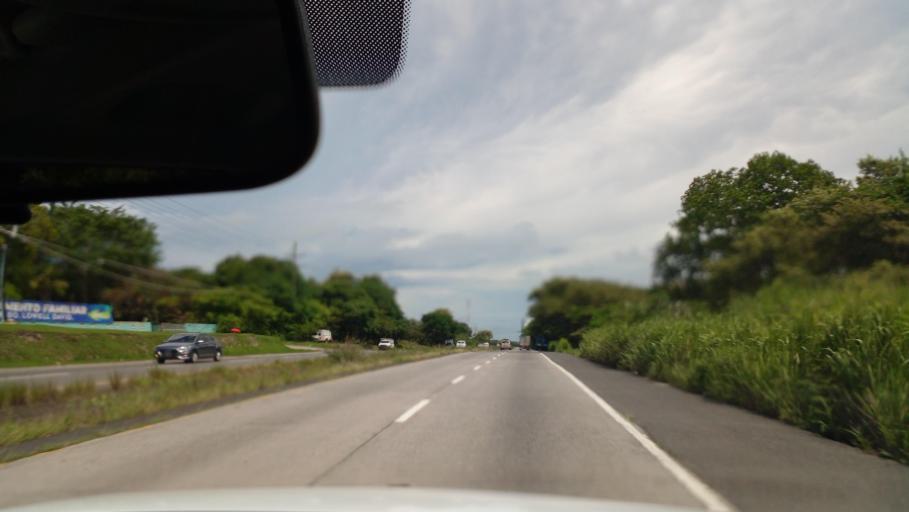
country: PA
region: Panama
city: Nueva Gorgona
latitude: 8.4863
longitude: -79.9582
